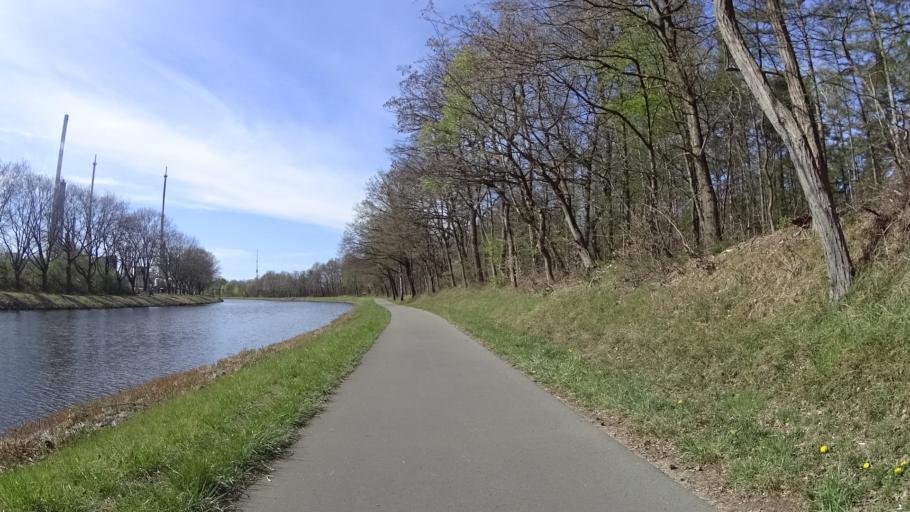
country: DE
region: Lower Saxony
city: Lingen
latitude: 52.5662
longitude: 7.3040
